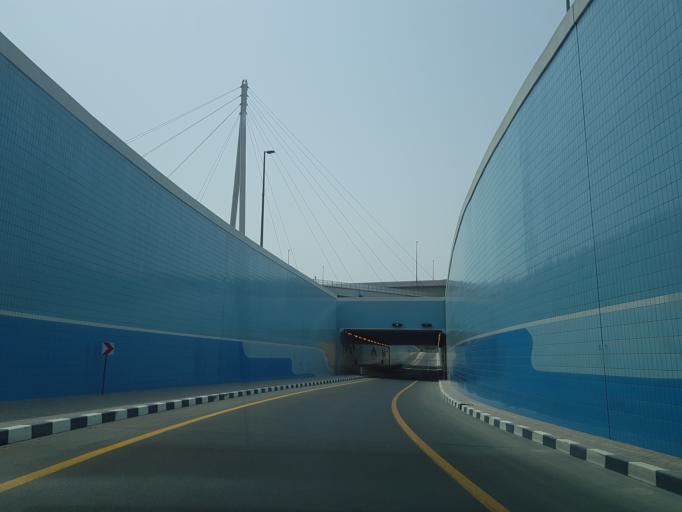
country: AE
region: Ash Shariqah
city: Sharjah
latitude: 25.2325
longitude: 55.2980
